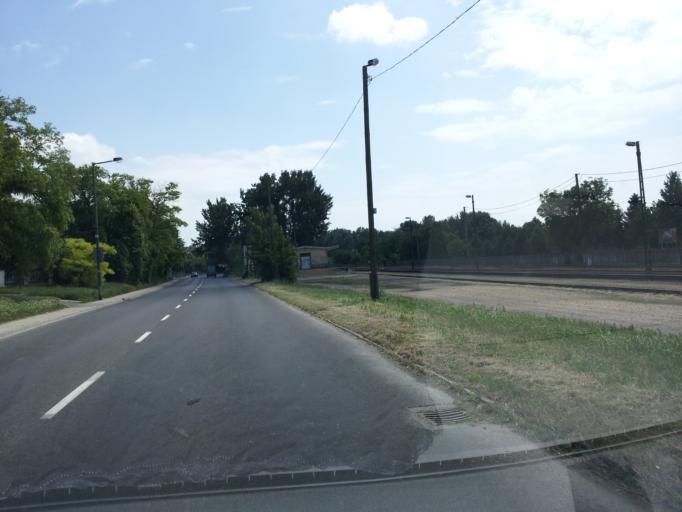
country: HU
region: Veszprem
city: Balatonalmadi
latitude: 47.0613
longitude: 18.0415
